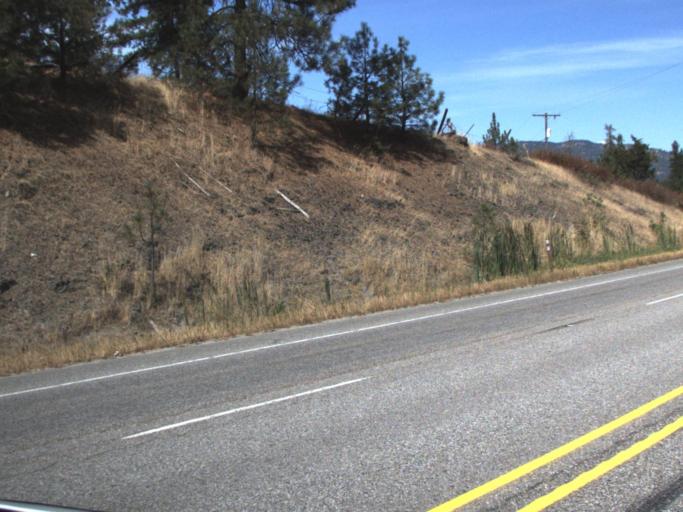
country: US
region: Washington
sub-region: Stevens County
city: Chewelah
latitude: 48.1898
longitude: -117.7007
